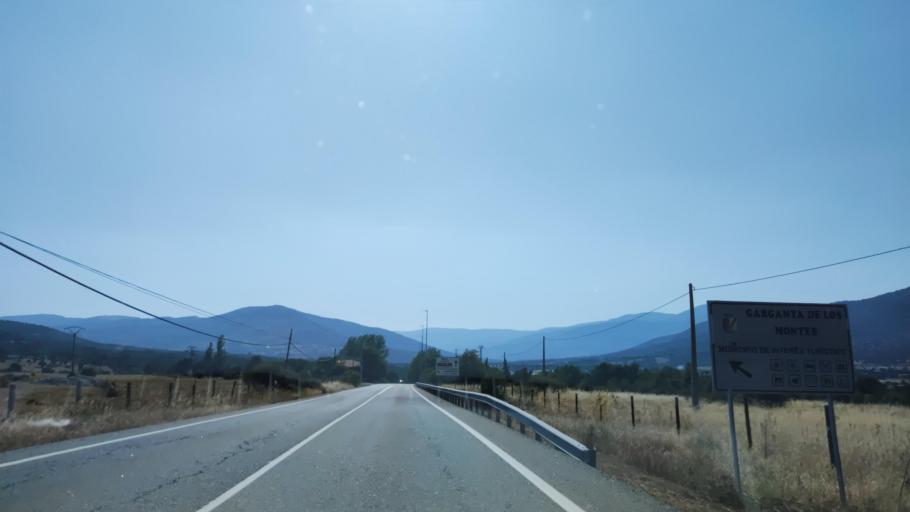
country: ES
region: Madrid
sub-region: Provincia de Madrid
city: Garganta de los Montes
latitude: 40.9423
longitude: -3.6971
